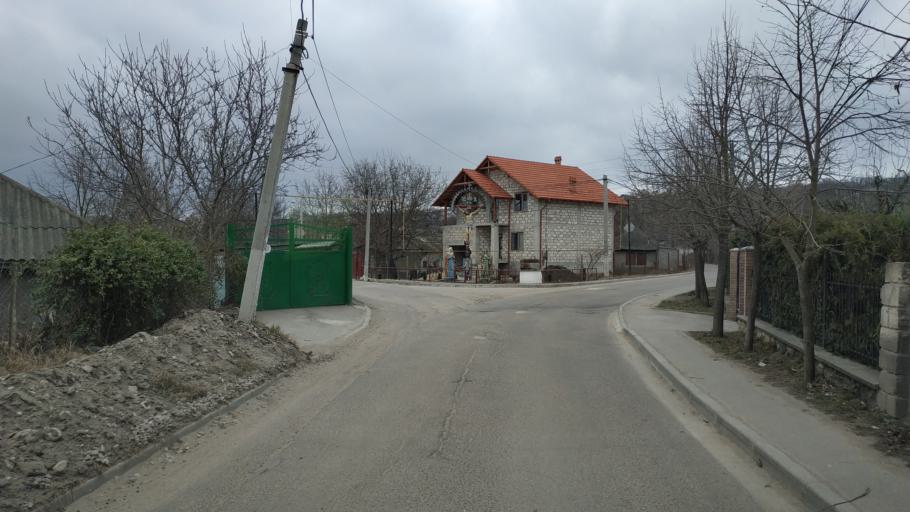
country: MD
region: Laloveni
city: Ialoveni
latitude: 46.9379
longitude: 28.7747
